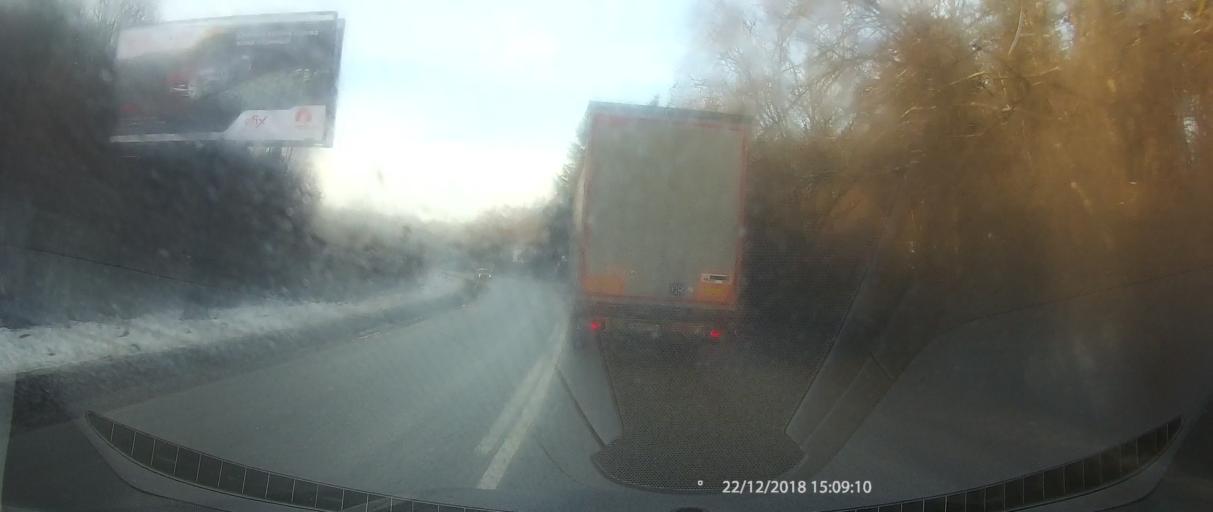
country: BG
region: Ruse
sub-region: Obshtina Borovo
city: Borovo
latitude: 43.4995
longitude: 25.8013
